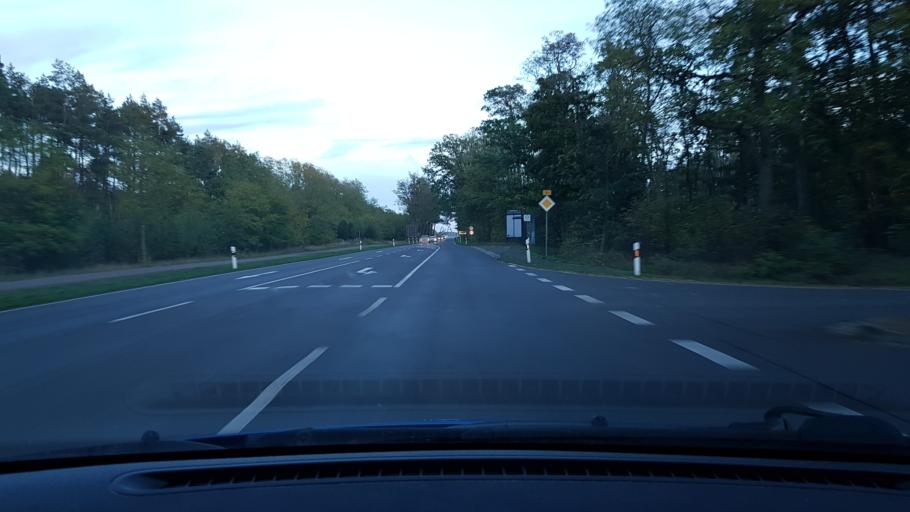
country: DE
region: Saxony-Anhalt
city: Wahlitz
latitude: 52.0894
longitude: 11.8014
